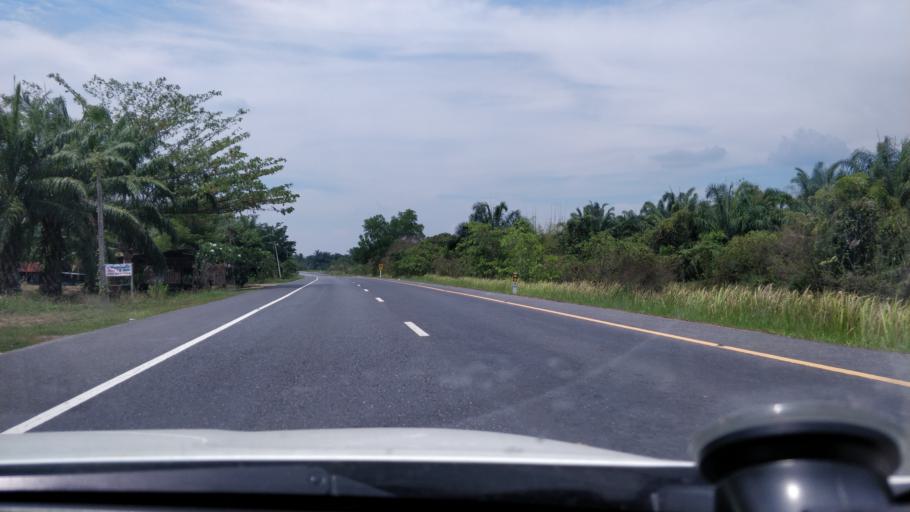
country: TH
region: Surat Thani
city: Khian Sa
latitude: 8.7275
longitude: 99.1591
